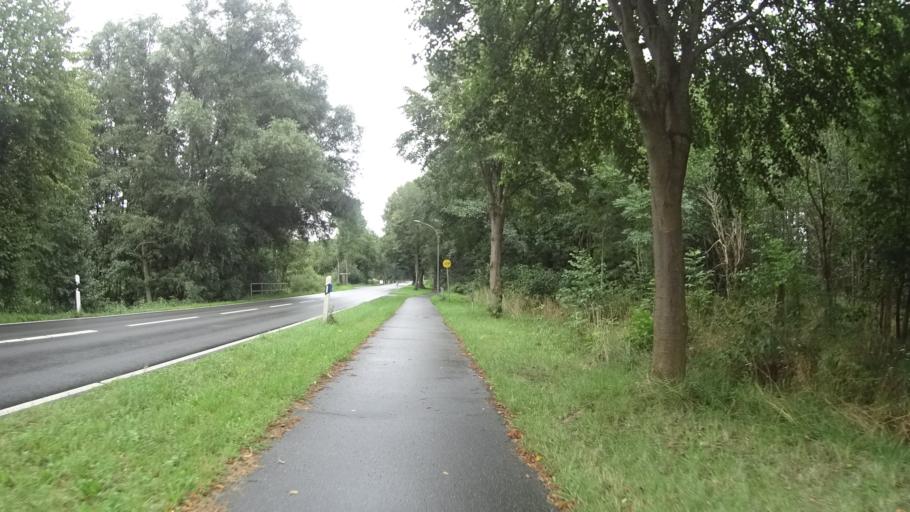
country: DE
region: Schleswig-Holstein
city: Alveslohe
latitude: 53.7856
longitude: 9.9437
